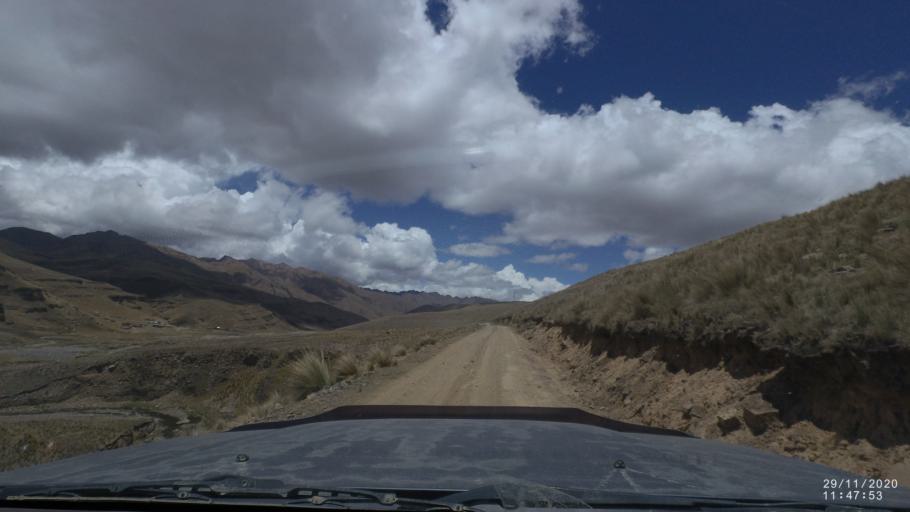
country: BO
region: Cochabamba
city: Cochabamba
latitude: -17.1816
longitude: -66.2545
